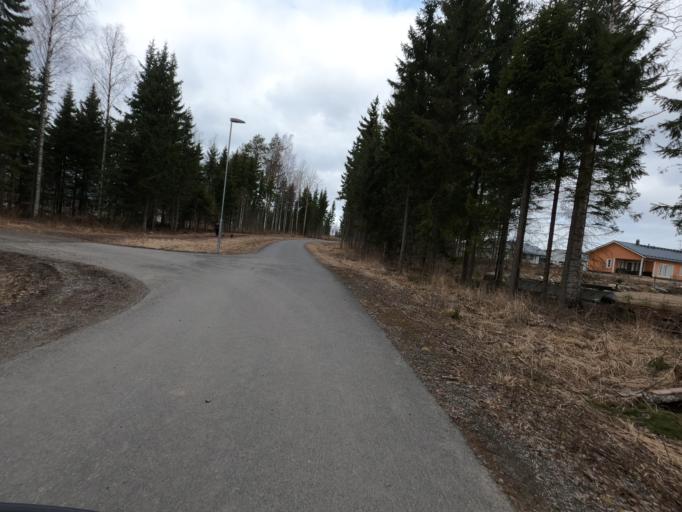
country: FI
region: North Karelia
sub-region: Joensuu
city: Joensuu
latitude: 62.5630
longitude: 29.8216
